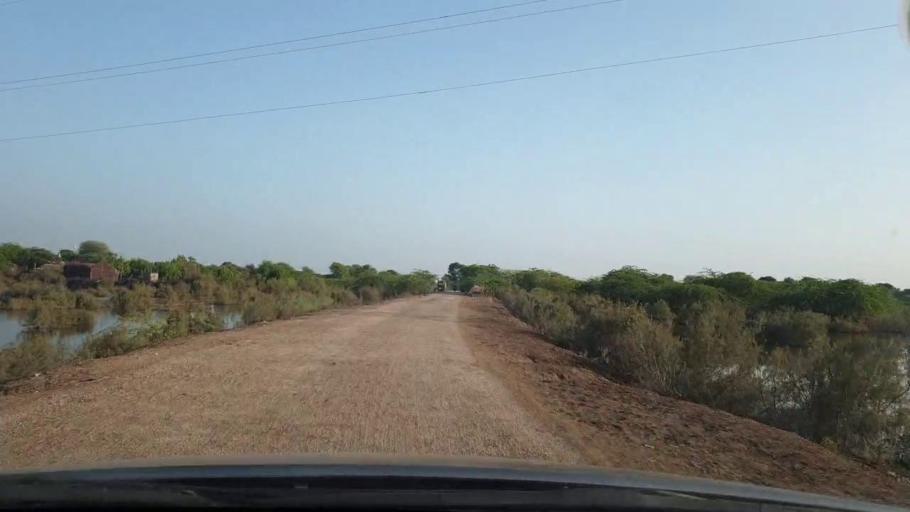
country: PK
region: Sindh
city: Naukot
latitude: 24.7695
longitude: 69.2027
